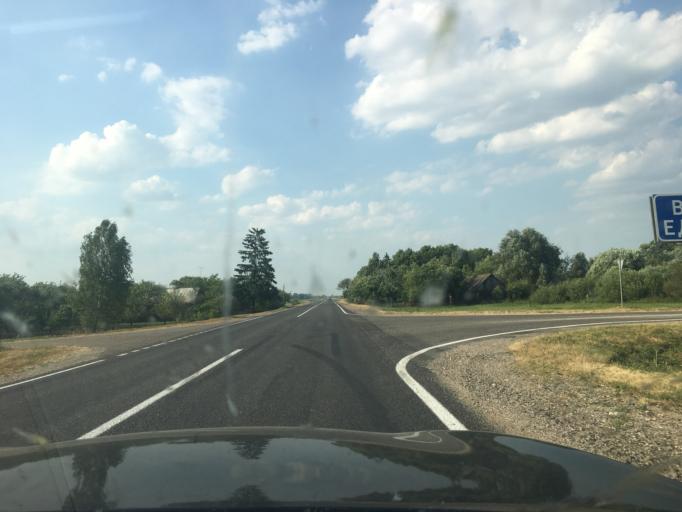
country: BY
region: Grodnenskaya
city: Indura
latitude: 53.3886
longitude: 23.9512
